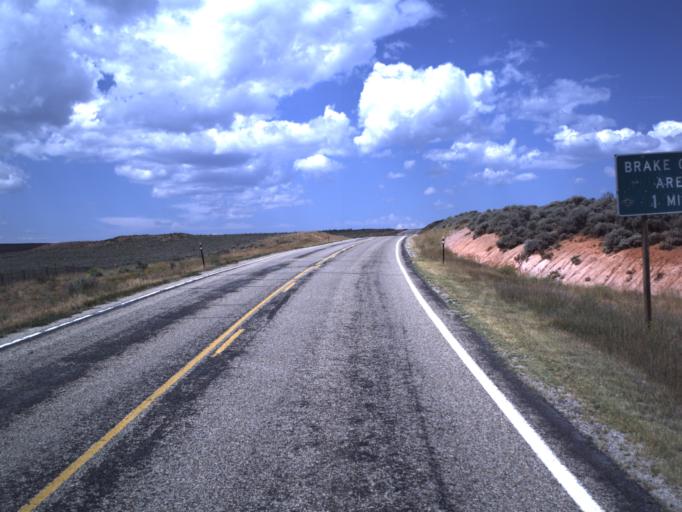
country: US
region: Utah
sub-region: Rich County
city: Randolph
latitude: 41.7954
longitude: -111.2323
